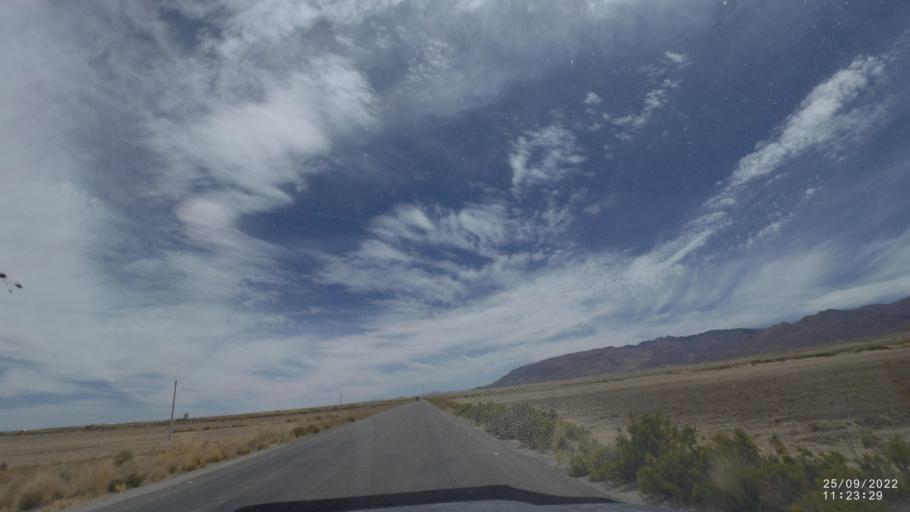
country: BO
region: Oruro
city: Challapata
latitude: -19.1086
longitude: -66.7710
